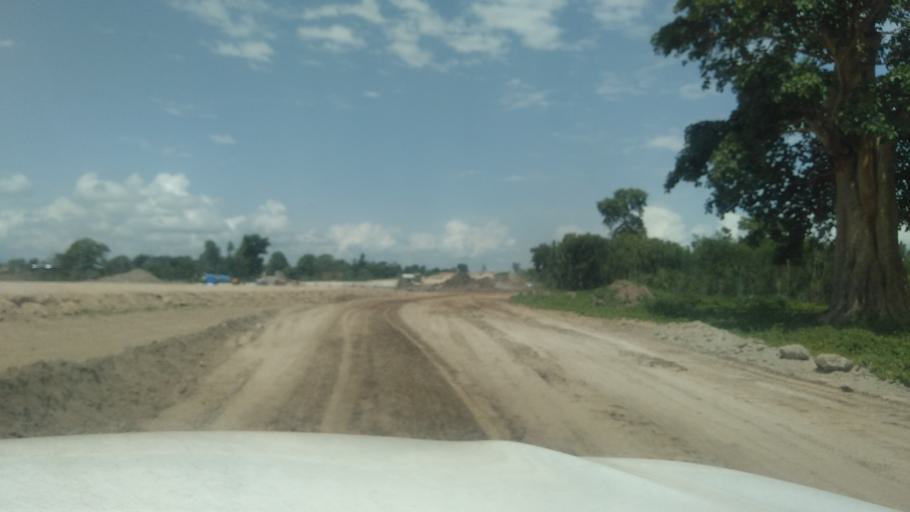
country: ET
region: Oromiya
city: Shashemene
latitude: 7.2811
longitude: 38.6055
